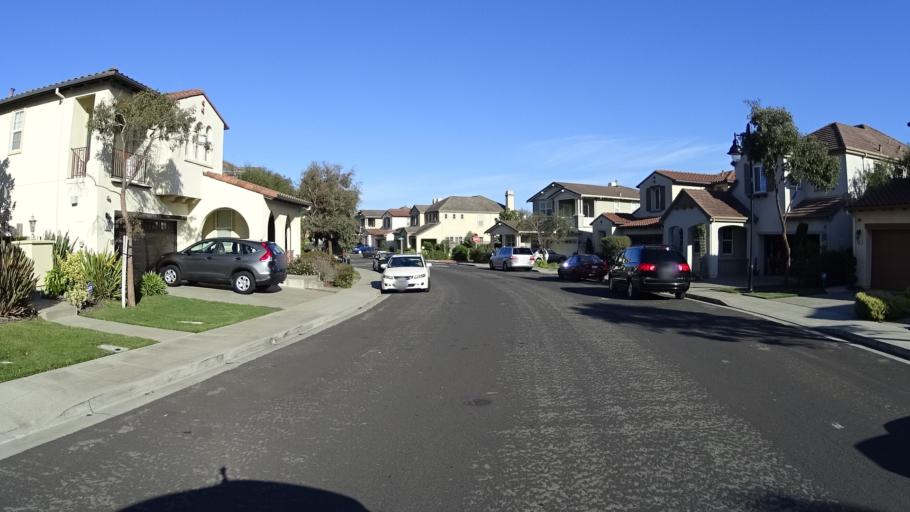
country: US
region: California
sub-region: San Mateo County
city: Pacifica
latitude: 37.6333
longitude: -122.4634
